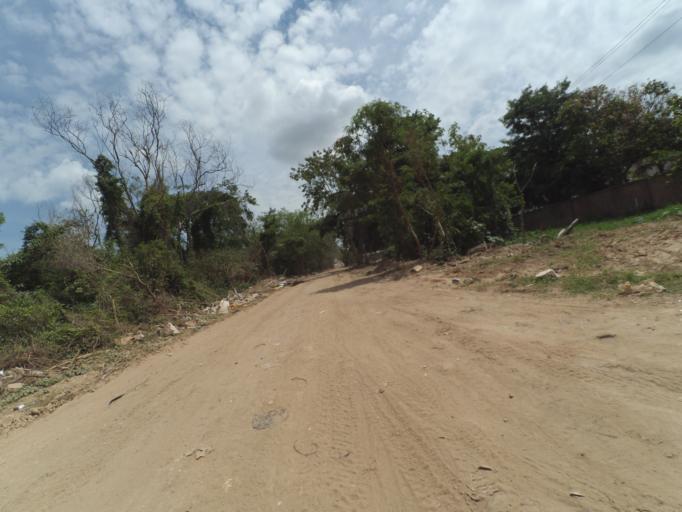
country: BO
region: Santa Cruz
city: Santa Cruz de la Sierra
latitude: -17.7879
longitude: -63.2242
